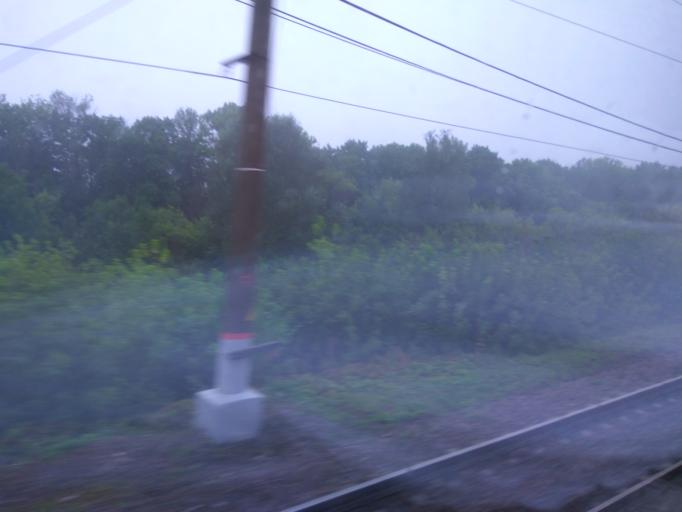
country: RU
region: Moskovskaya
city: Uzunovo
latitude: 54.5628
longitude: 38.6212
